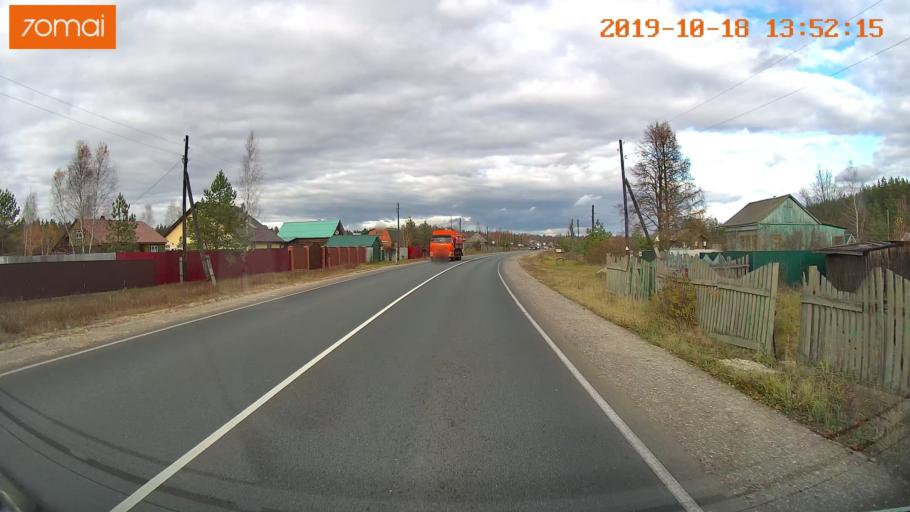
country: RU
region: Moskovskaya
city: Radovitskiy
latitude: 55.0280
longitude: 39.9666
